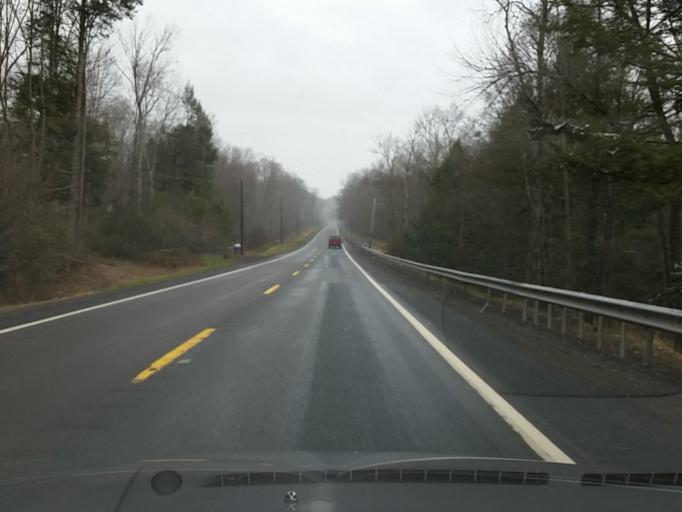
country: US
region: Pennsylvania
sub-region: Sullivan County
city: Laporte
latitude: 41.2860
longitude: -76.3262
